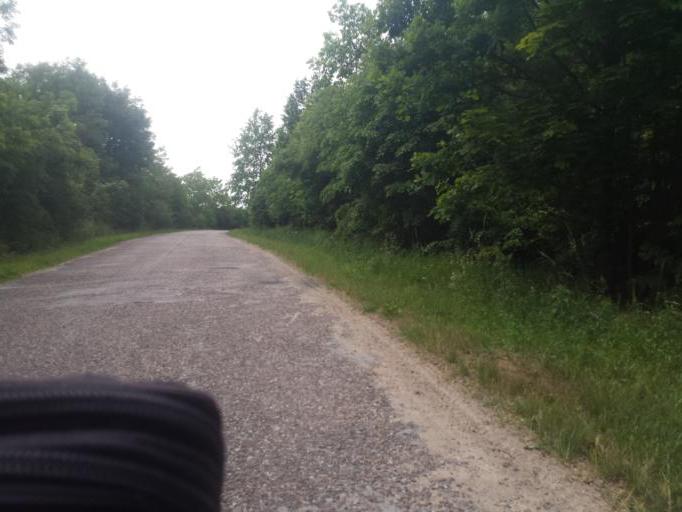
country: PL
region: Warmian-Masurian Voivodeship
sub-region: Powiat ilawski
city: Ilawa
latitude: 53.5229
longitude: 19.5475
